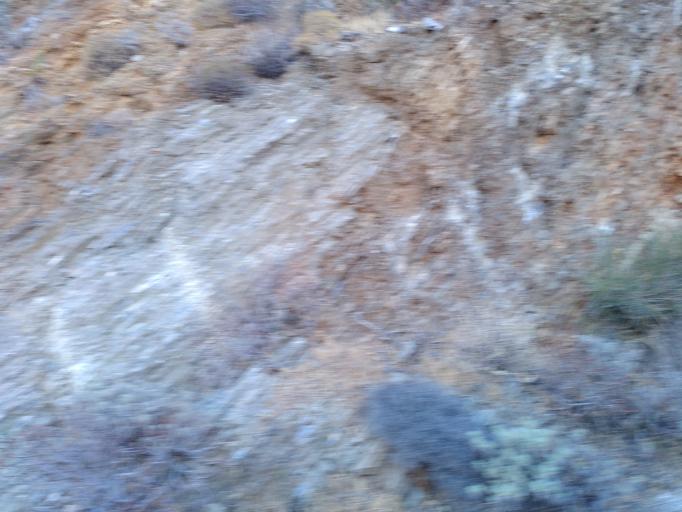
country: GR
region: South Aegean
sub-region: Nomos Kykladon
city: Amorgos
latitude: 36.9119
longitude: 25.9773
